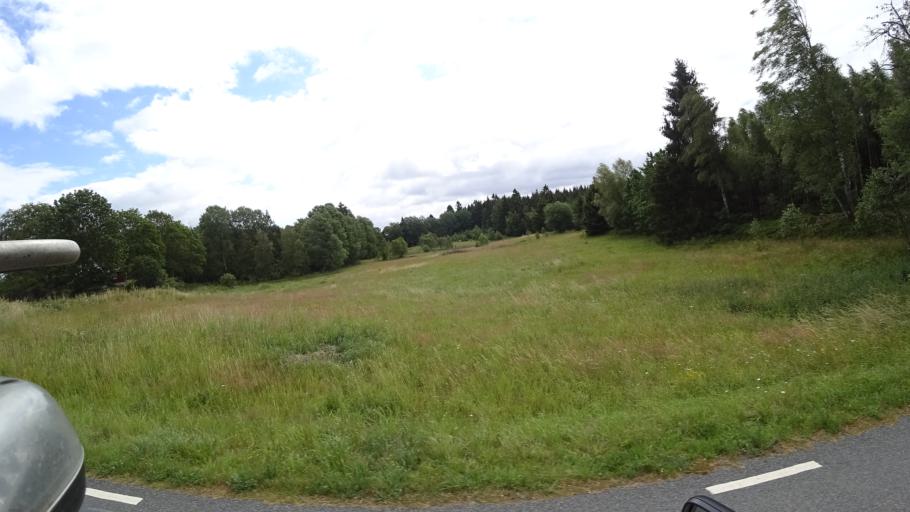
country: SE
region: Skane
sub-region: Kristianstads Kommun
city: Degeberga
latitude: 55.7249
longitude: 13.9976
